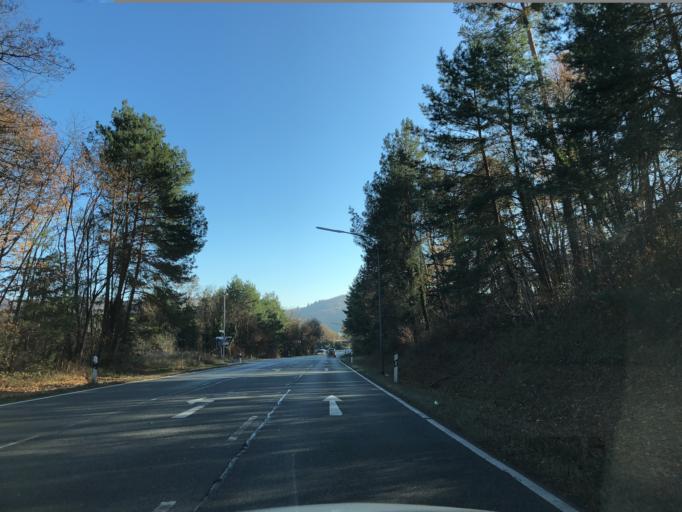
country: DE
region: Hesse
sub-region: Regierungsbezirk Darmstadt
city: Bickenbach
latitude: 49.7639
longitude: 8.6282
